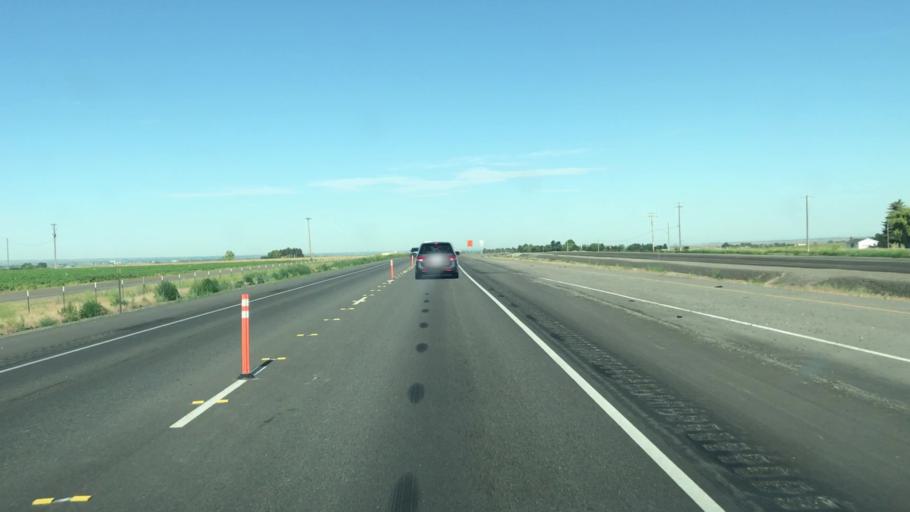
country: US
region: Idaho
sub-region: Twin Falls County
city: Hansen
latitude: 42.5762
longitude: -114.2667
